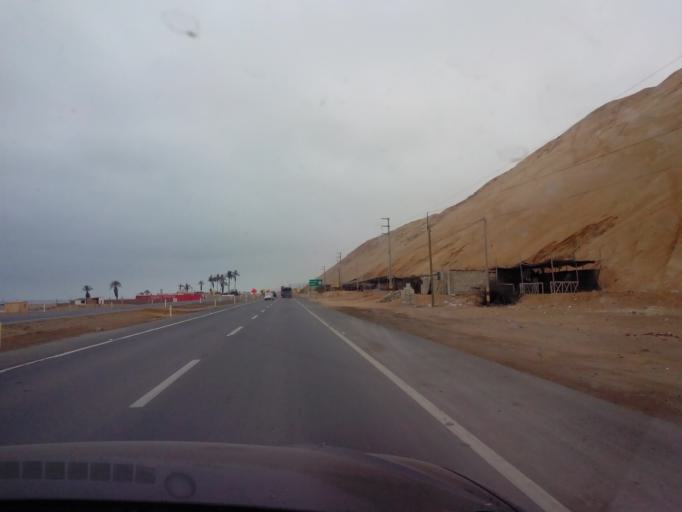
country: PE
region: Ica
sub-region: Provincia de Chincha
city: San Pedro
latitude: -13.3316
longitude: -76.2374
